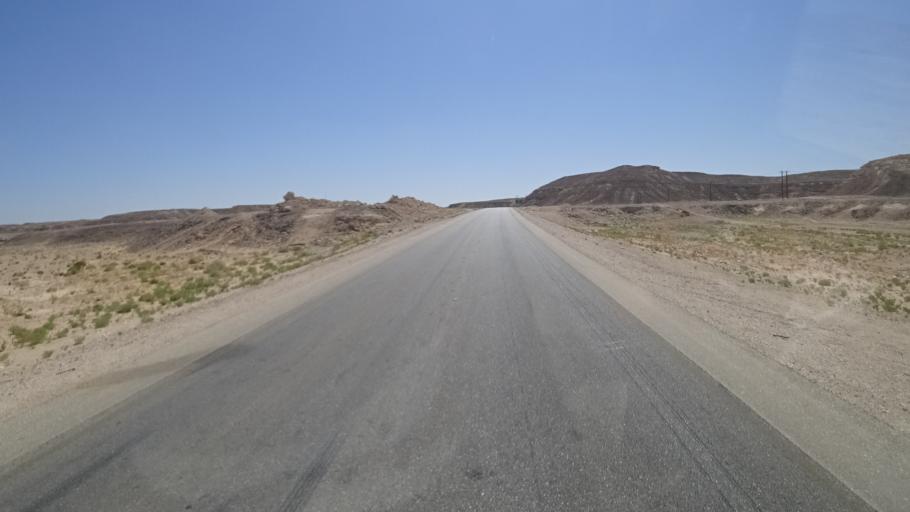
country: OM
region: Zufar
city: Salalah
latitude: 17.5031
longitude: 53.3632
